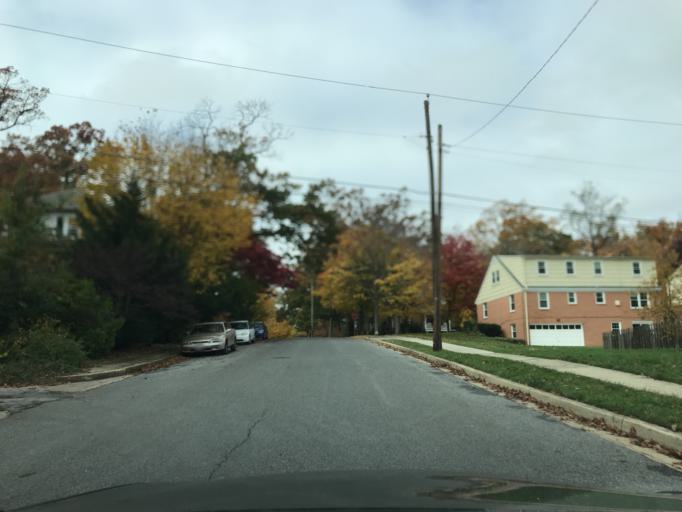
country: US
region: Maryland
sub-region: Baltimore County
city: Towson
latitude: 39.3784
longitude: -76.5969
